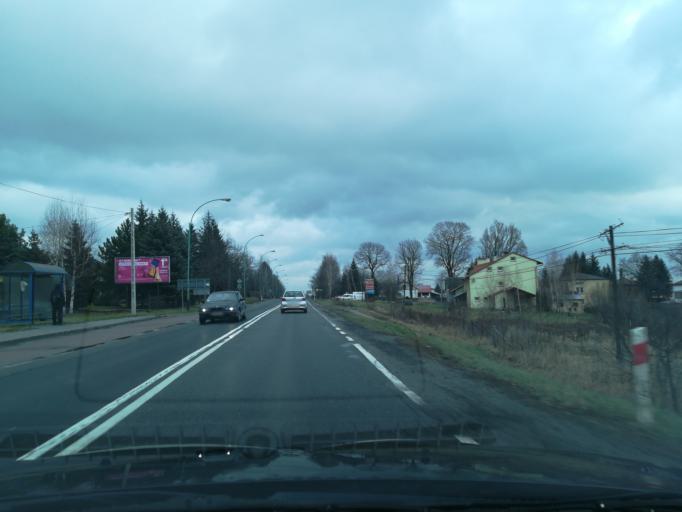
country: PL
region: Subcarpathian Voivodeship
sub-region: Powiat lancucki
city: Sonina
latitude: 50.0740
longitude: 22.2514
